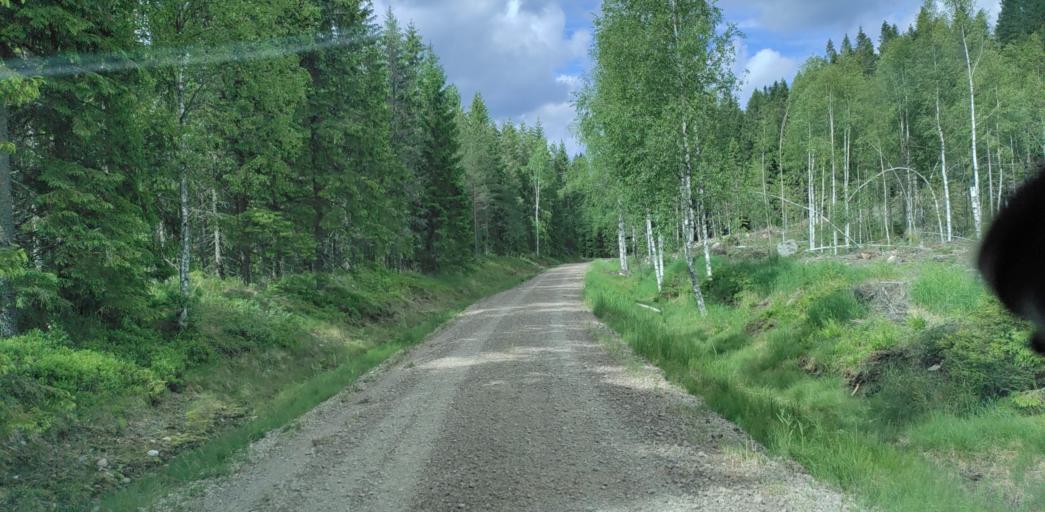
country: SE
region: Vaermland
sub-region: Munkfors Kommun
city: Munkfors
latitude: 59.9523
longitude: 13.4120
